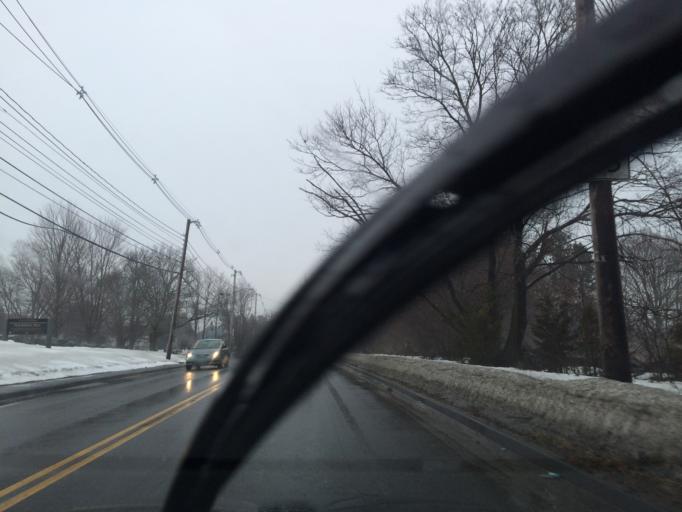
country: US
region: Massachusetts
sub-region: Middlesex County
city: Belmont
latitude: 42.3962
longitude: -71.2086
